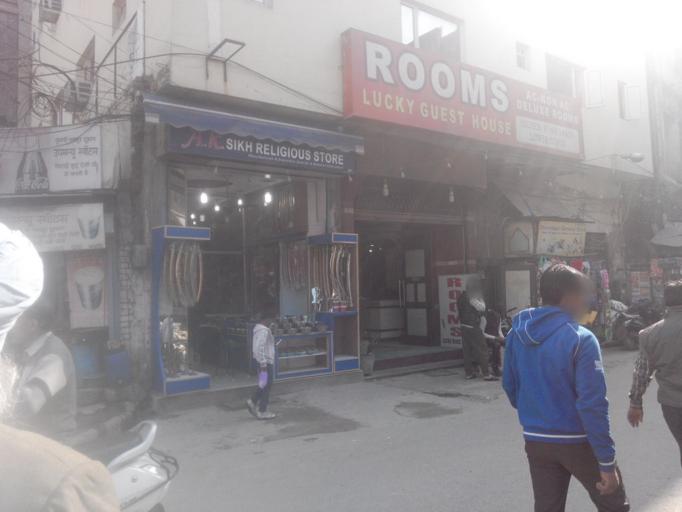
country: IN
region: Punjab
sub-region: Amritsar
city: Amritsar
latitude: 31.6229
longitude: 74.8788
